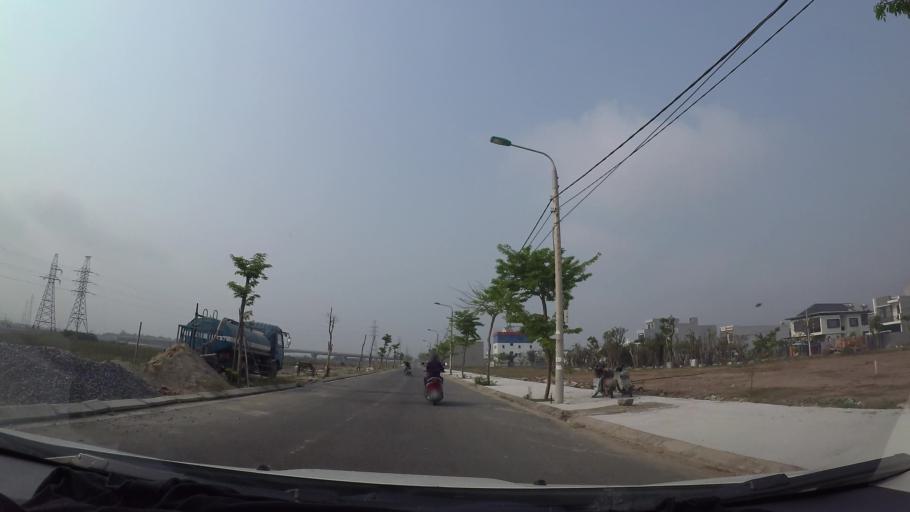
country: VN
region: Da Nang
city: Ngu Hanh Son
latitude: 16.0064
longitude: 108.2298
